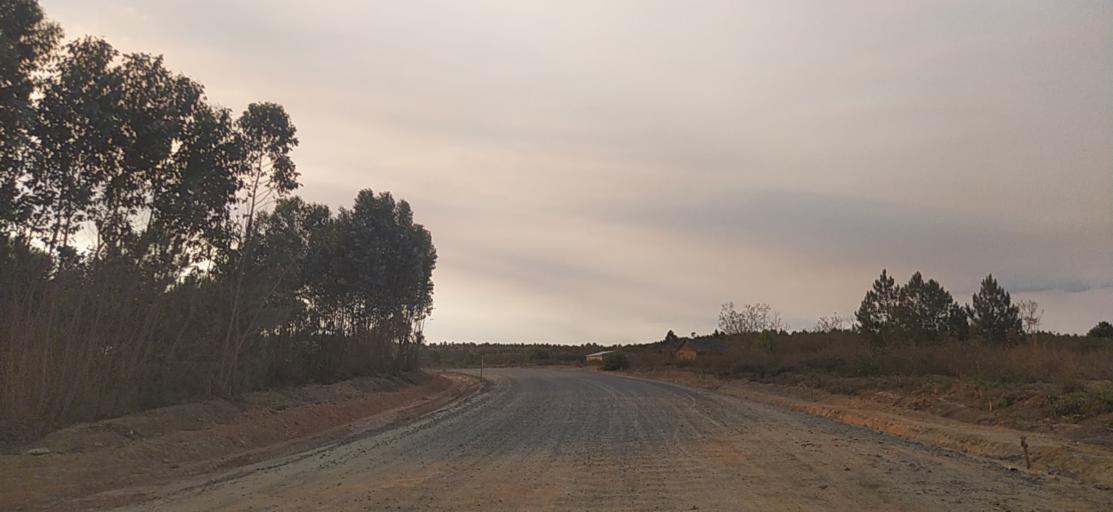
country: MG
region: Analamanga
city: Anjozorobe
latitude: -18.5003
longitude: 48.2675
